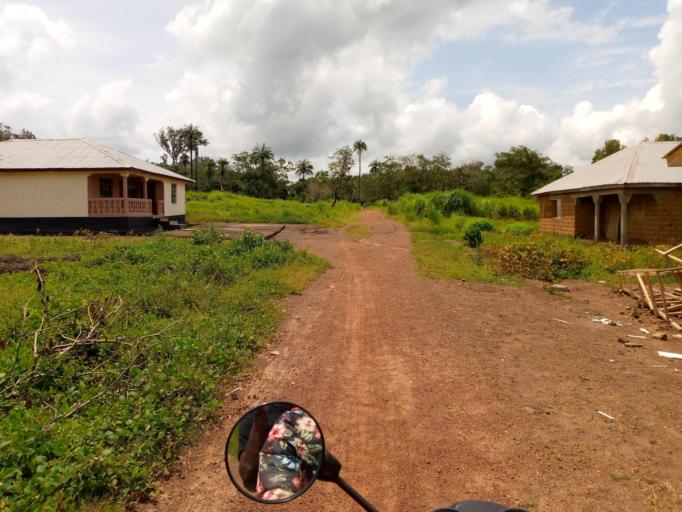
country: SL
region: Northern Province
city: Binkolo
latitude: 9.1221
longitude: -12.1333
